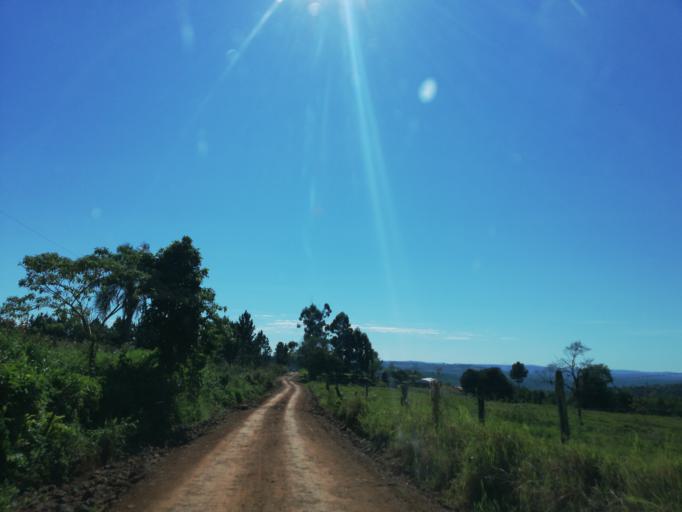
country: AR
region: Misiones
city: Dos de Mayo
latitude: -27.0763
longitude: -54.4013
